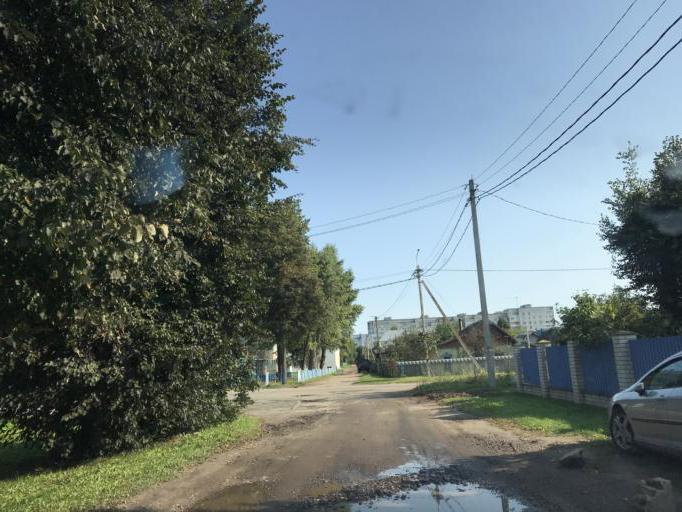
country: BY
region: Mogilev
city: Buynichy
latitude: 53.8810
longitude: 30.2708
